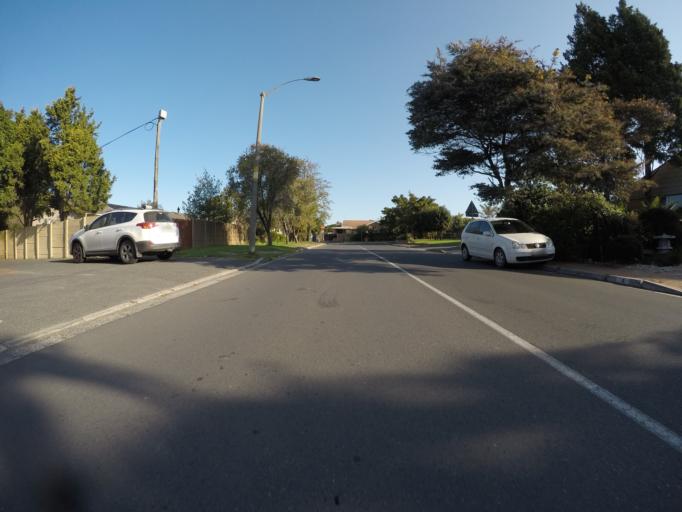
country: ZA
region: Western Cape
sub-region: City of Cape Town
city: Kraaifontein
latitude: -33.8548
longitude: 18.6573
